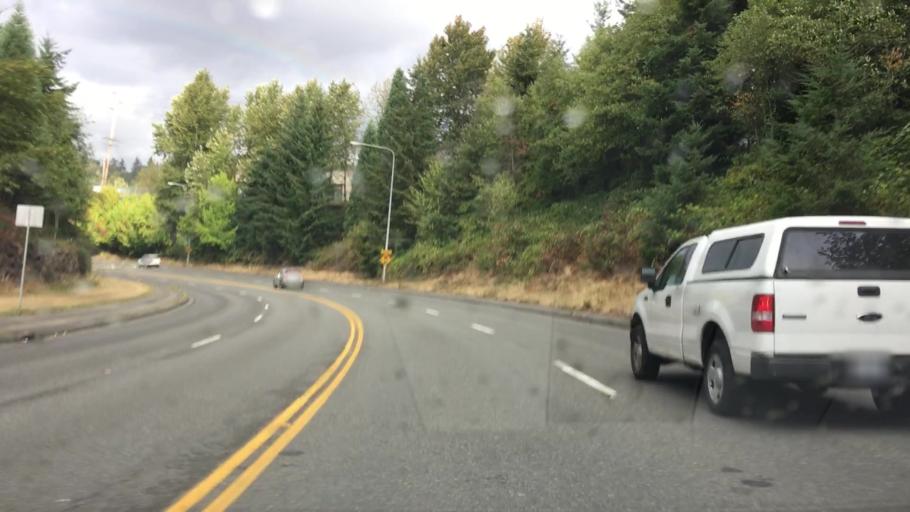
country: US
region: Washington
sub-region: King County
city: Woodinville
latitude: 47.7681
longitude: -122.1511
